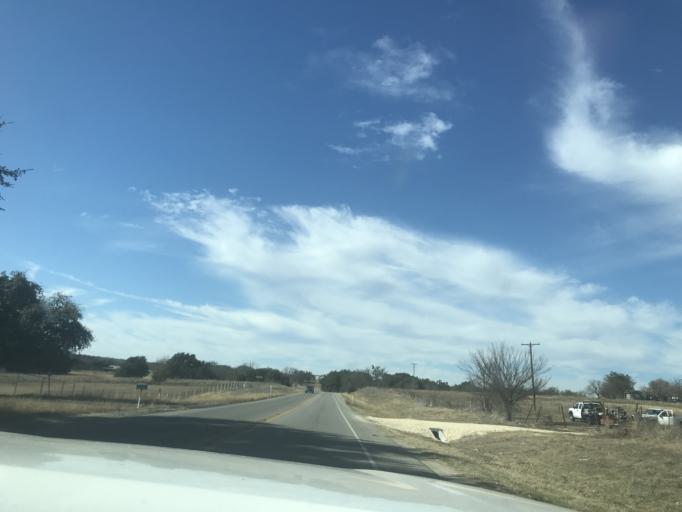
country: US
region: Texas
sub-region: Erath County
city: Stephenville
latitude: 32.2037
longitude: -98.1854
